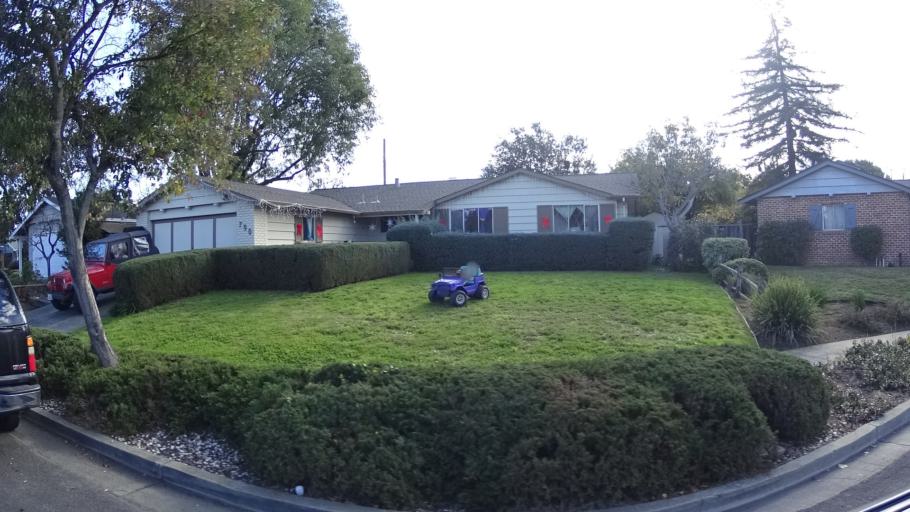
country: US
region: California
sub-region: Santa Clara County
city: Sunnyvale
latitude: 37.3508
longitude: -122.0457
